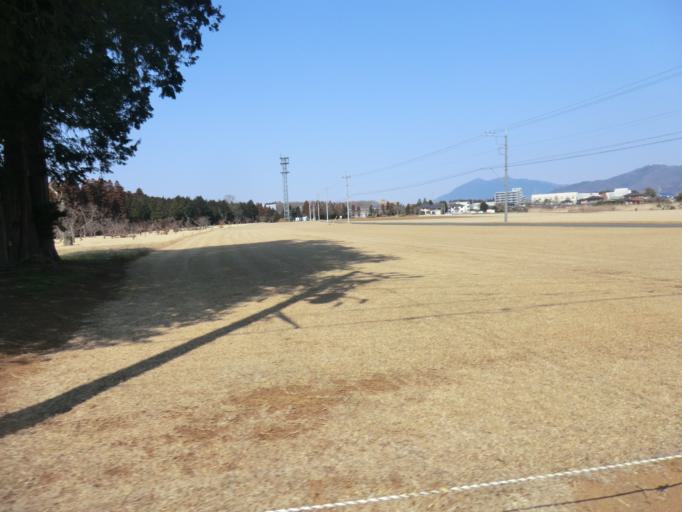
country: JP
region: Ibaraki
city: Naka
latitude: 36.1071
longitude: 140.1183
